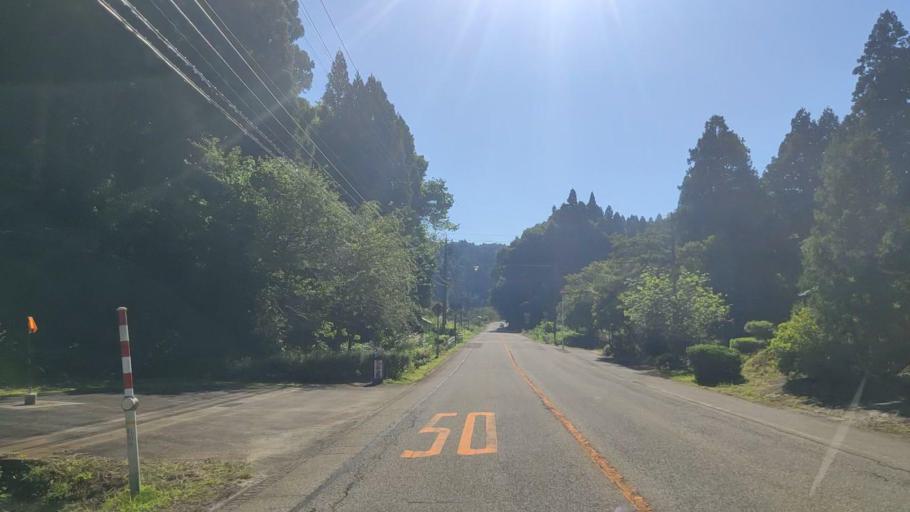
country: JP
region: Ishikawa
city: Nanao
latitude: 37.3238
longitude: 137.1916
